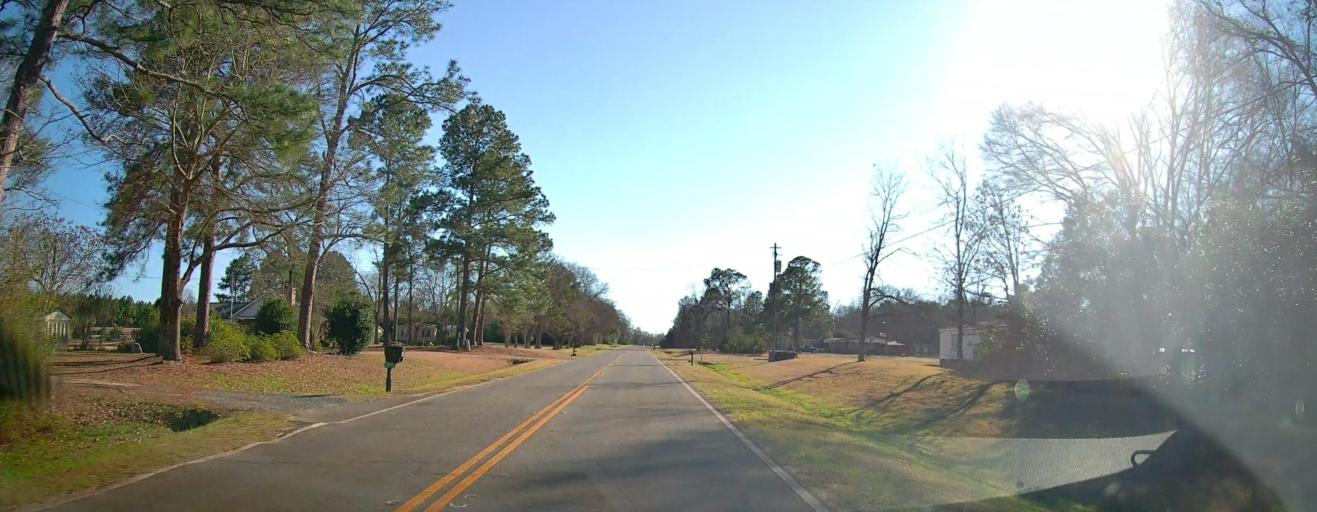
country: US
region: Georgia
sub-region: Sumter County
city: Americus
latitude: 32.0547
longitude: -84.2714
